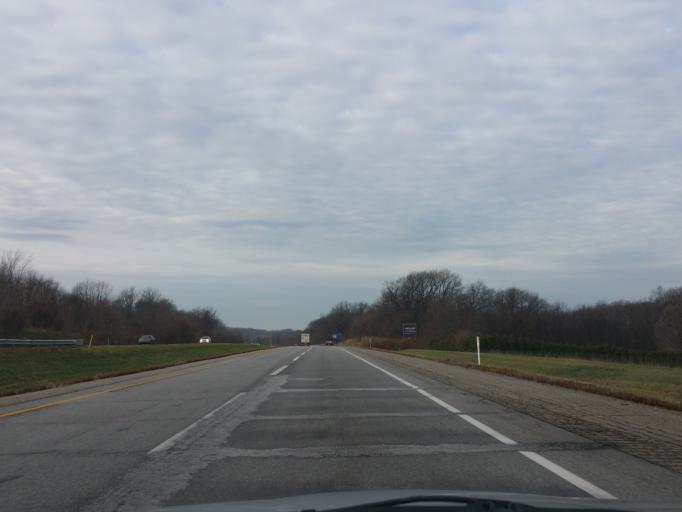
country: US
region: Indiana
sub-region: LaPorte County
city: LaPorte
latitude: 41.6745
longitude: -86.7010
